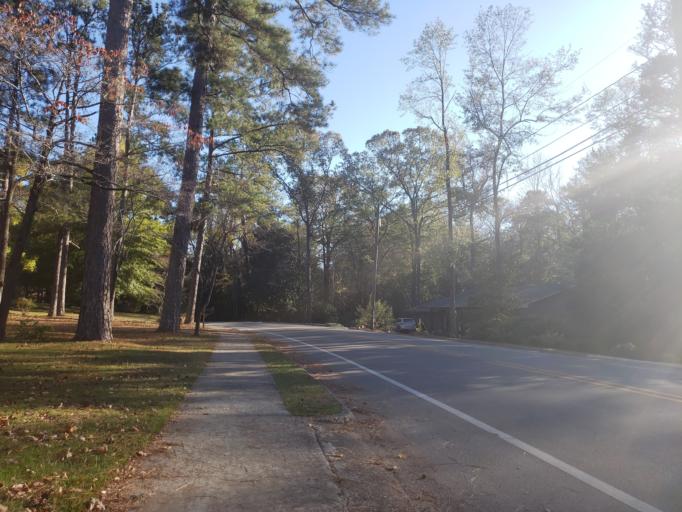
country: US
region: Alabama
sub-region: Lee County
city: Auburn
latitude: 32.5905
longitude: -85.4798
